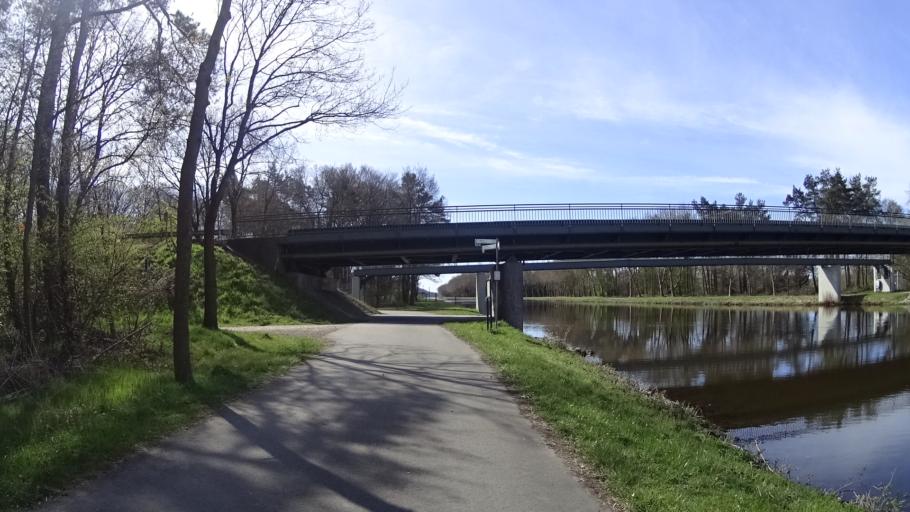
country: DE
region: Lower Saxony
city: Geeste
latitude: 52.5989
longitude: 7.3093
